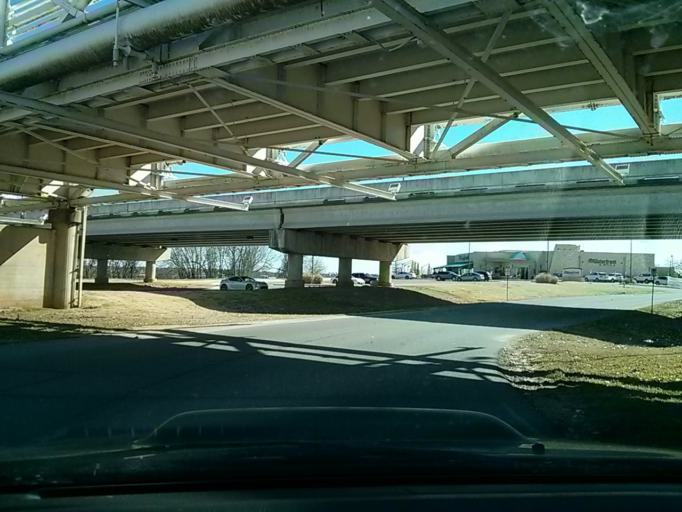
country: US
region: Oklahoma
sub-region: Tulsa County
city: Jenks
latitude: 36.0244
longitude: -95.9580
